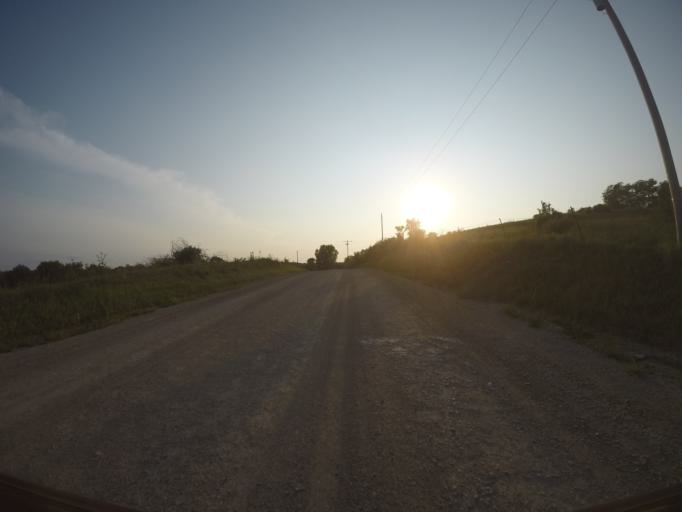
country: US
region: Kansas
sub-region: Riley County
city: Manhattan
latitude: 39.1289
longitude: -96.4759
